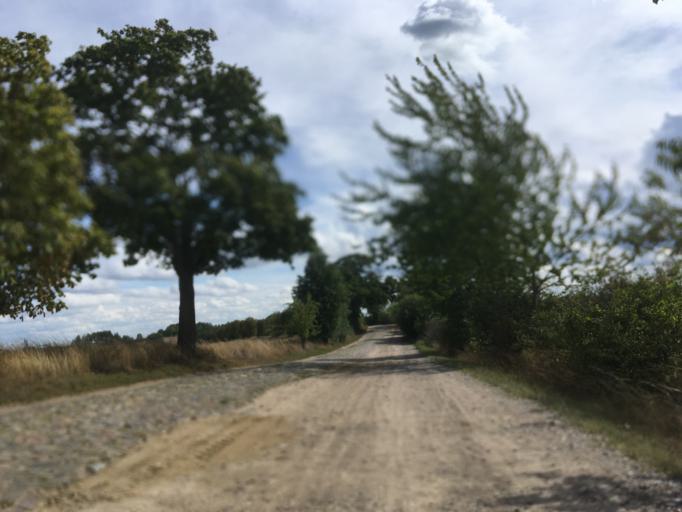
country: DE
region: Brandenburg
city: Gerswalde
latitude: 53.1285
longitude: 13.8010
